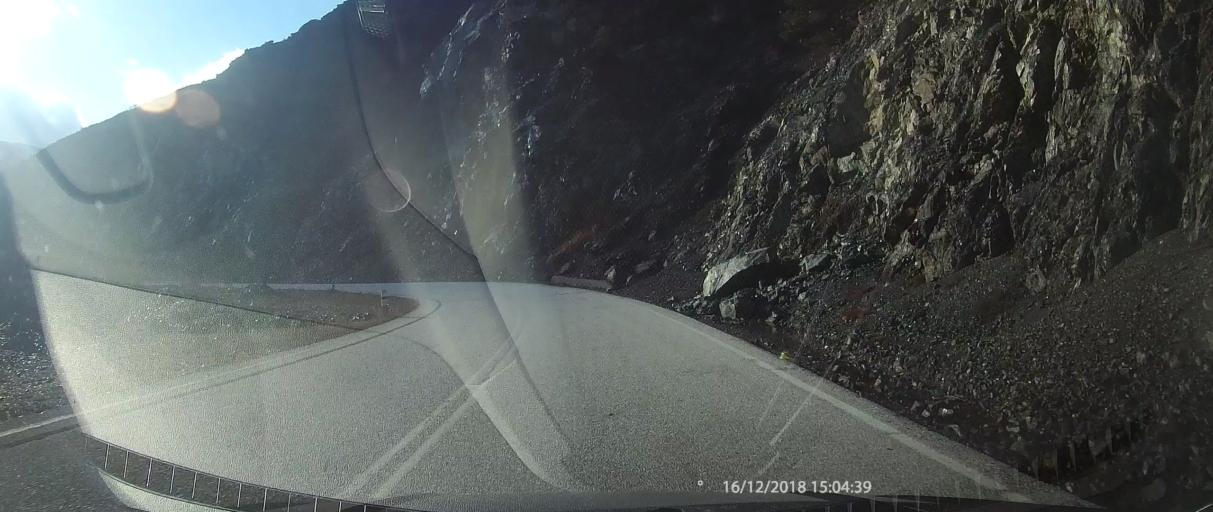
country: GR
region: West Macedonia
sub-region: Nomos Kastorias
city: Nestorio
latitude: 40.2285
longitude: 20.9659
